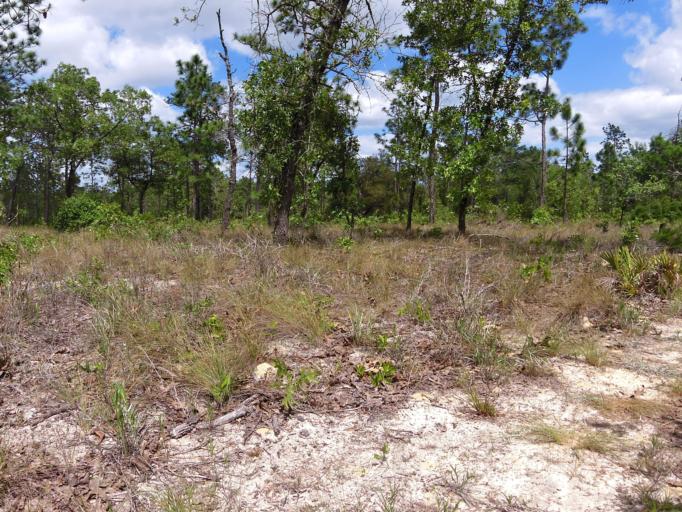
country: US
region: Florida
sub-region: Clay County
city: Keystone Heights
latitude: 29.8365
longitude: -81.9746
